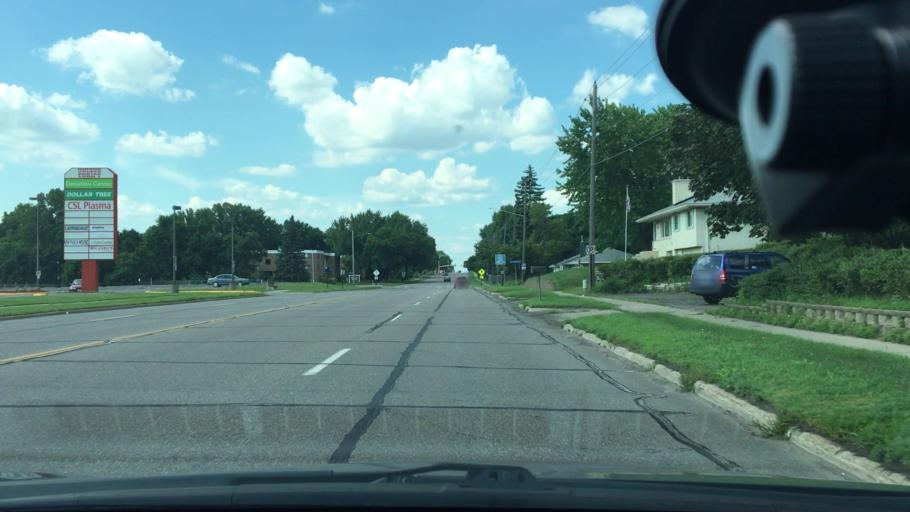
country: US
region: Minnesota
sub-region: Hennepin County
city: New Hope
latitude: 45.0350
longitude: -93.3803
